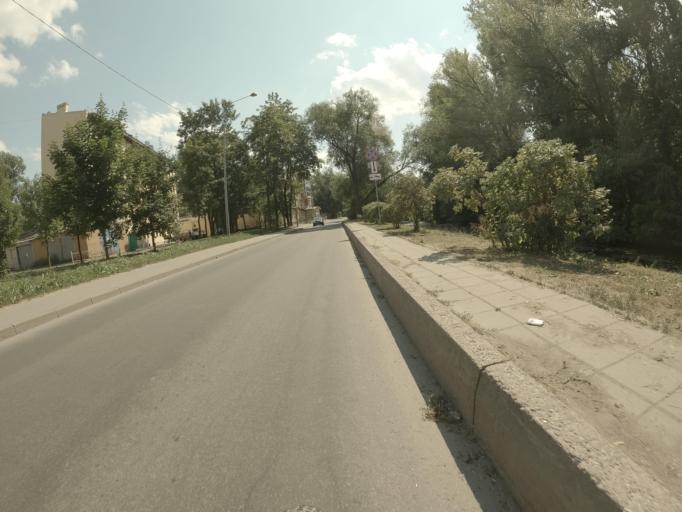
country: RU
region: St.-Petersburg
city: Admiralteisky
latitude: 59.9036
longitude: 30.2689
